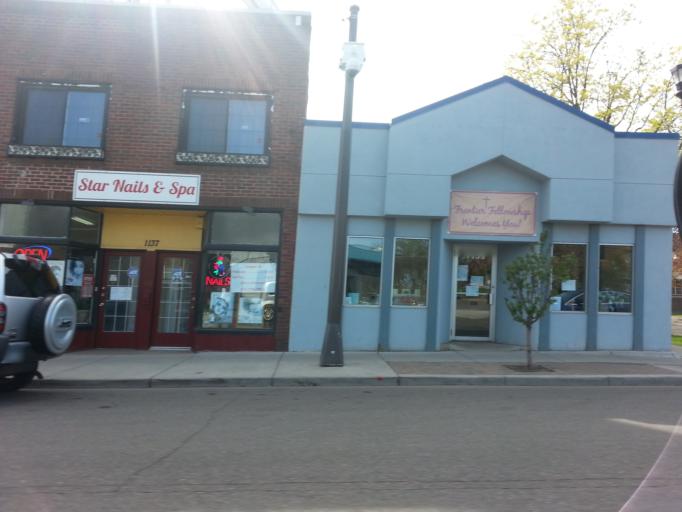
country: US
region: Minnesota
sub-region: Ramsey County
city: Saint Paul
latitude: 44.9754
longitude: -93.0735
